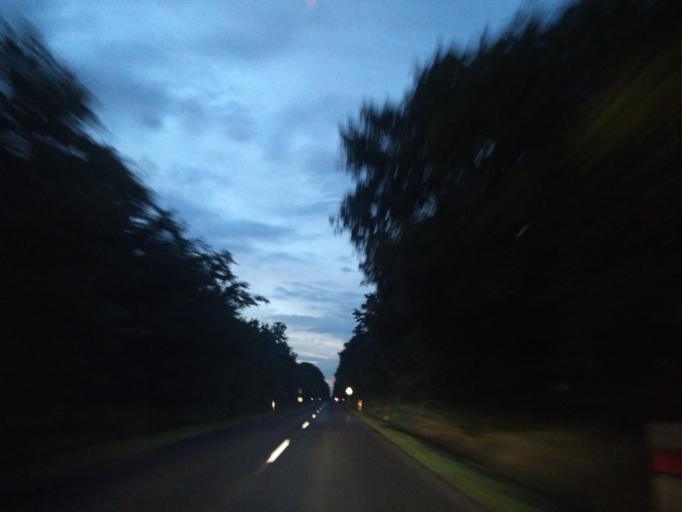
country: HU
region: Fejer
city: Lovasbereny
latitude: 47.3265
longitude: 18.5728
